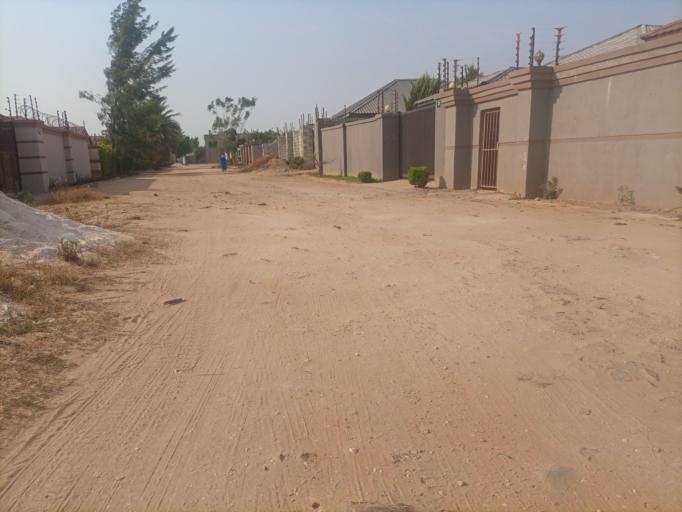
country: ZM
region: Lusaka
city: Lusaka
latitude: -15.3991
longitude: 28.3893
